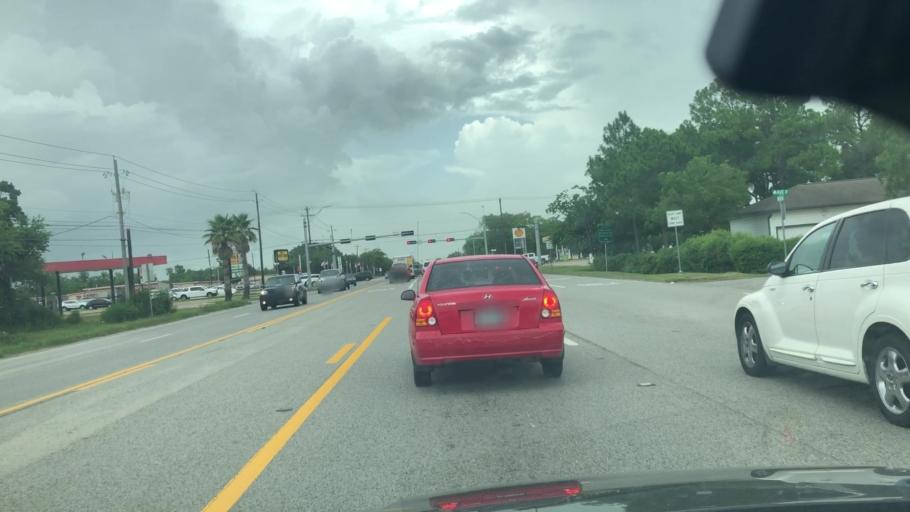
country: US
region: Texas
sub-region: Galveston County
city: Dickinson
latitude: 29.4797
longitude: -95.0709
